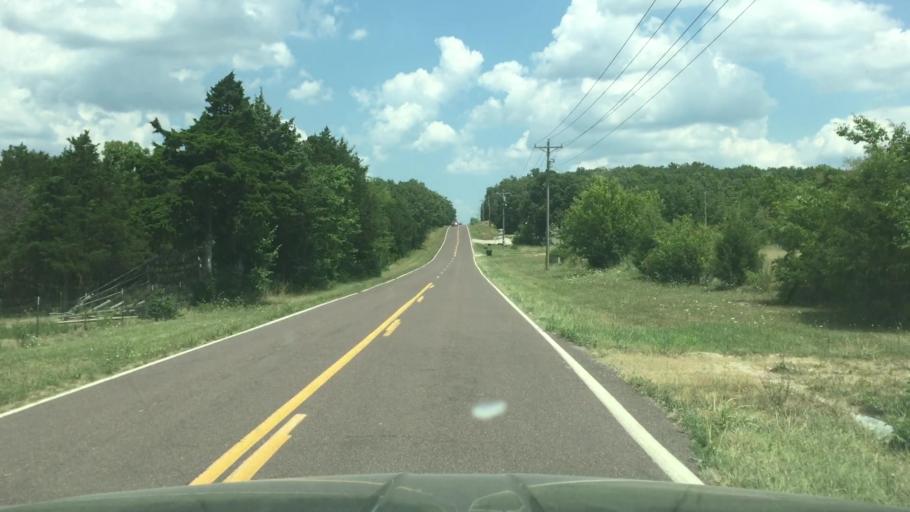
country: US
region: Missouri
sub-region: Miller County
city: Tuscumbia
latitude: 38.1099
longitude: -92.4729
